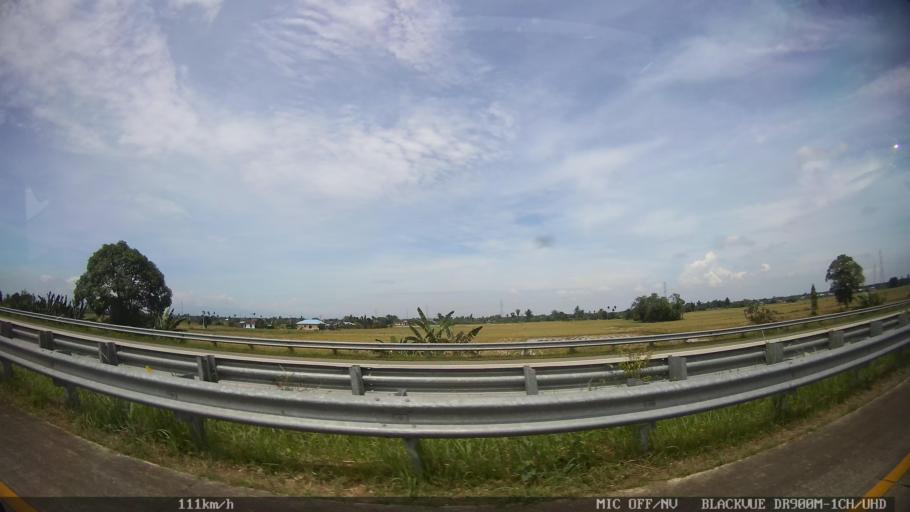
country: ID
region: North Sumatra
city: Percut
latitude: 3.5750
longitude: 98.8471
